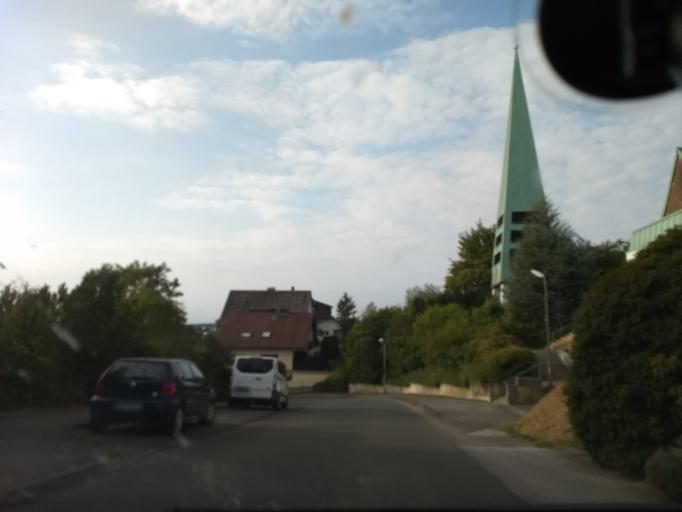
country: DE
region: North Rhine-Westphalia
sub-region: Regierungsbezirk Arnsberg
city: Arnsberg
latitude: 51.3908
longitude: 8.0796
